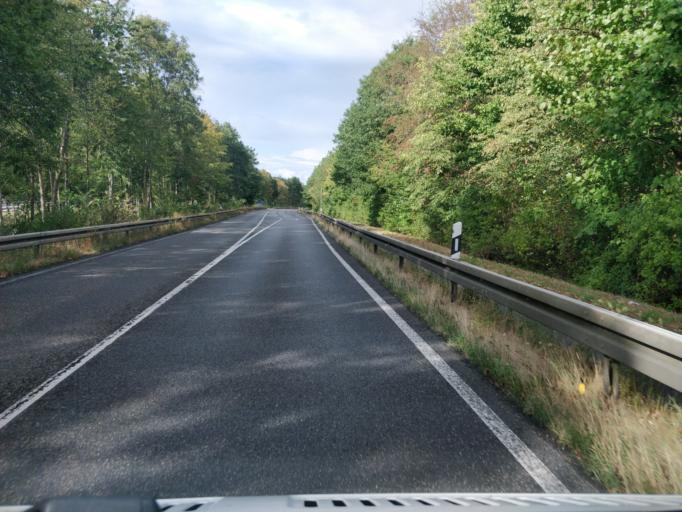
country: DE
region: North Rhine-Westphalia
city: Meckenheim
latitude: 50.6514
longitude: 7.0473
